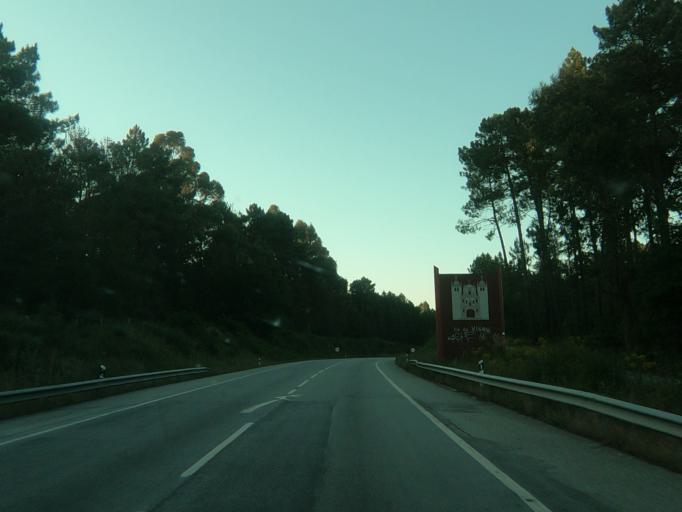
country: PT
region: Viseu
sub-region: Viseu
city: Rio de Loba
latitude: 40.6651
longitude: -7.8620
